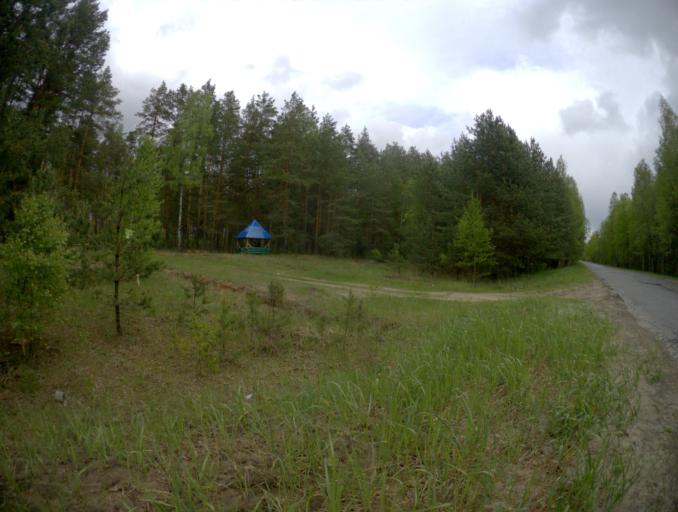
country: RU
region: Vladimir
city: Zolotkovo
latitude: 55.3515
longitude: 40.9244
